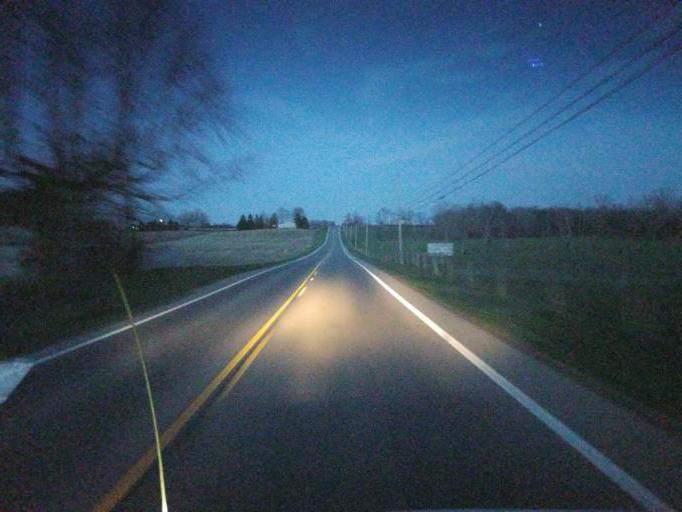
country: US
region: Ohio
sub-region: Logan County
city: Bellefontaine
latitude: 40.3647
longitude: -83.8168
